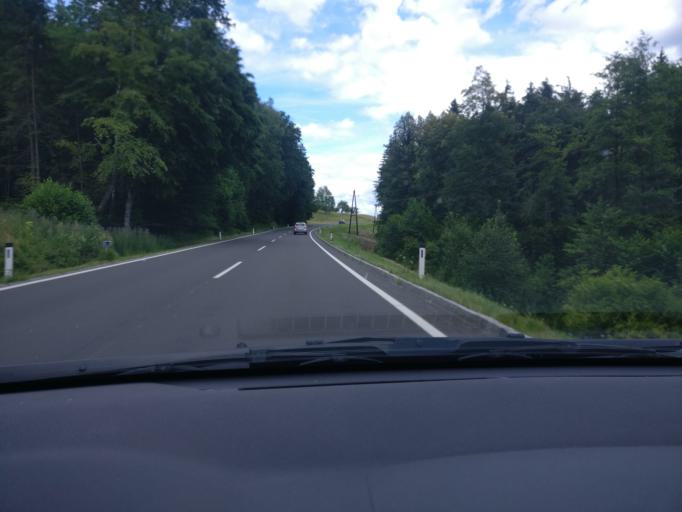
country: AT
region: Styria
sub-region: Politischer Bezirk Weiz
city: Oberrettenbach
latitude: 47.1624
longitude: 15.7757
